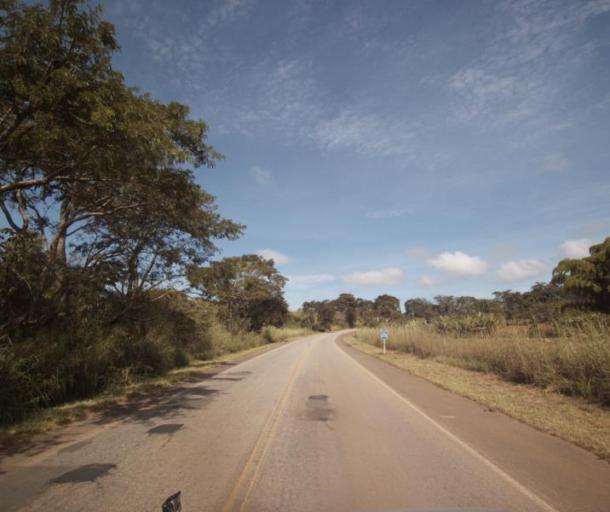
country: BR
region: Goias
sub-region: Abadiania
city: Abadiania
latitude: -16.1098
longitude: -48.8780
